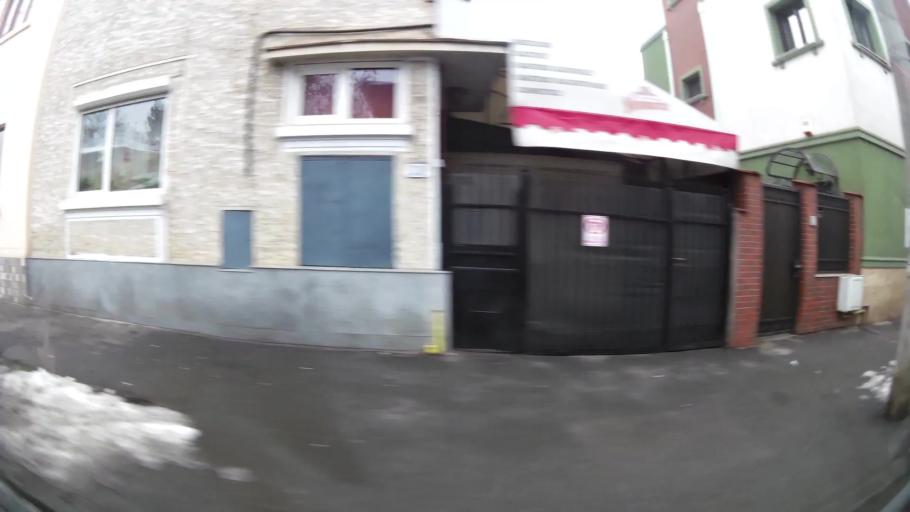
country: RO
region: Ilfov
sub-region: Comuna Chiajna
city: Rosu
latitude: 44.4507
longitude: 26.0548
